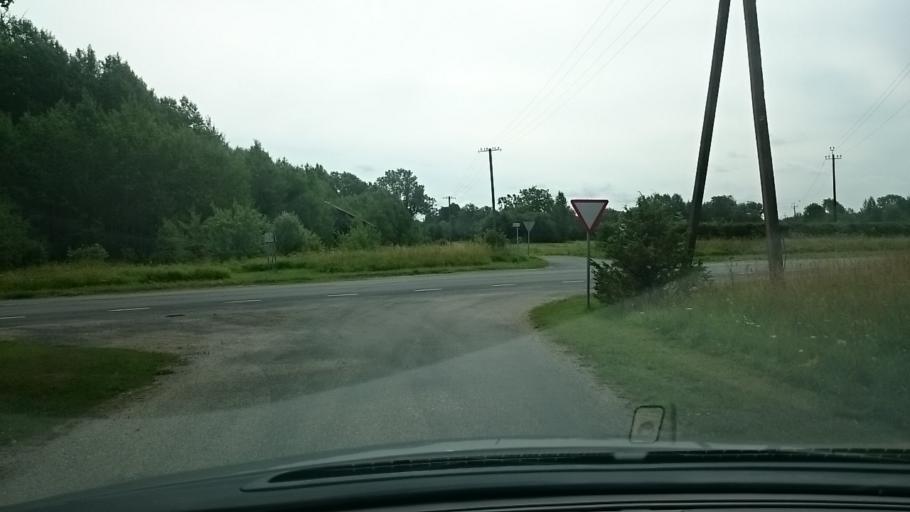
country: EE
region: Laeaene
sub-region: Ridala Parish
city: Uuemoisa
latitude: 58.9776
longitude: 23.6802
